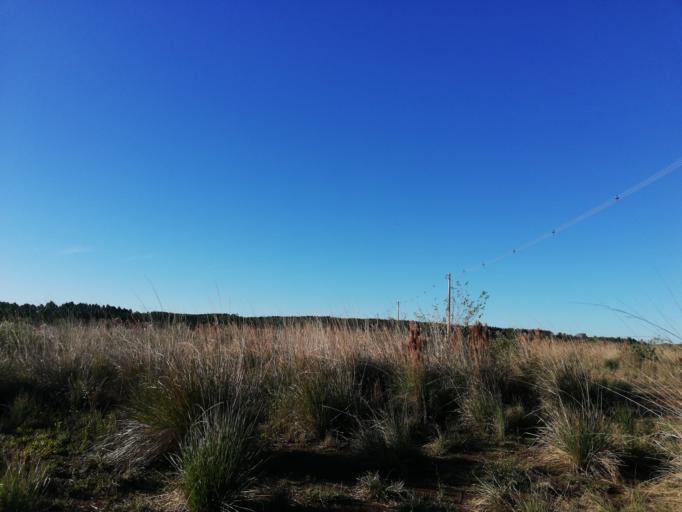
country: AR
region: Misiones
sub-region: Departamento de Candelaria
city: Candelaria
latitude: -27.4975
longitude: -55.7729
